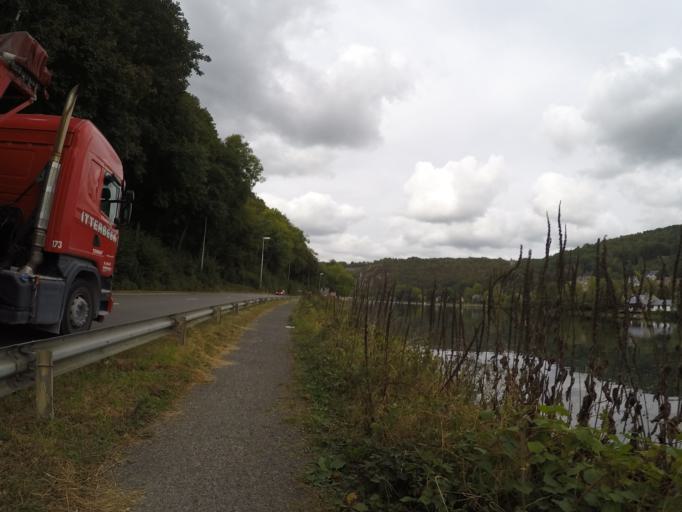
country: BE
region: Wallonia
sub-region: Province de Namur
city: Yvoir
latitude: 50.3282
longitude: 4.8710
